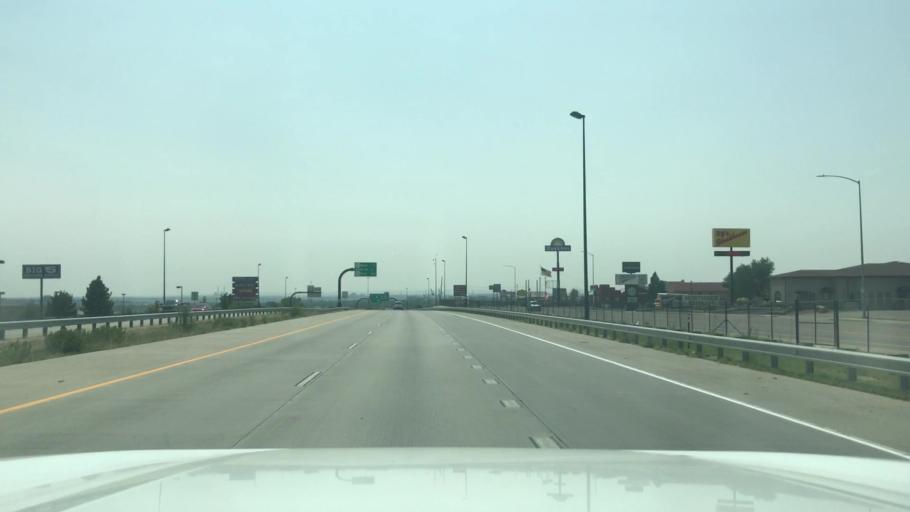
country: US
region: Colorado
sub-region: Pueblo County
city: Pueblo
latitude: 38.3159
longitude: -104.6155
